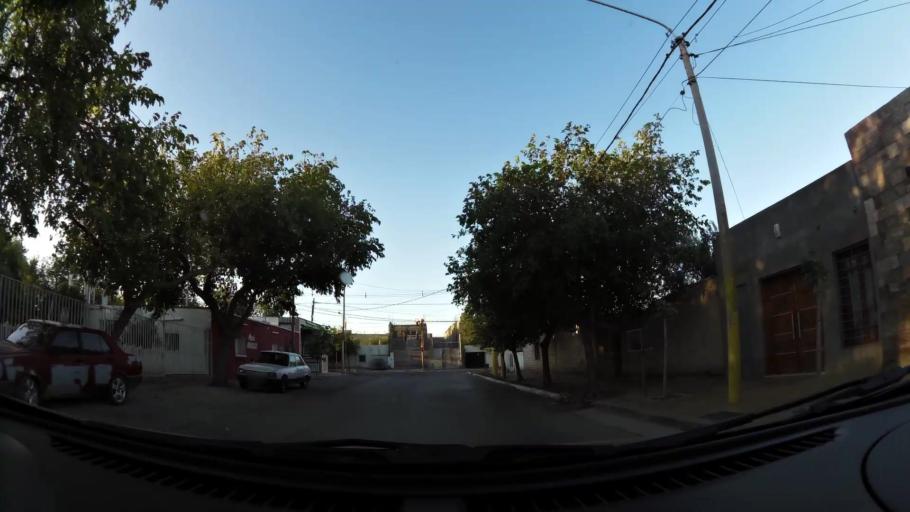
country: AR
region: San Juan
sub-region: Departamento de Santa Lucia
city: Santa Lucia
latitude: -31.5207
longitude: -68.5093
